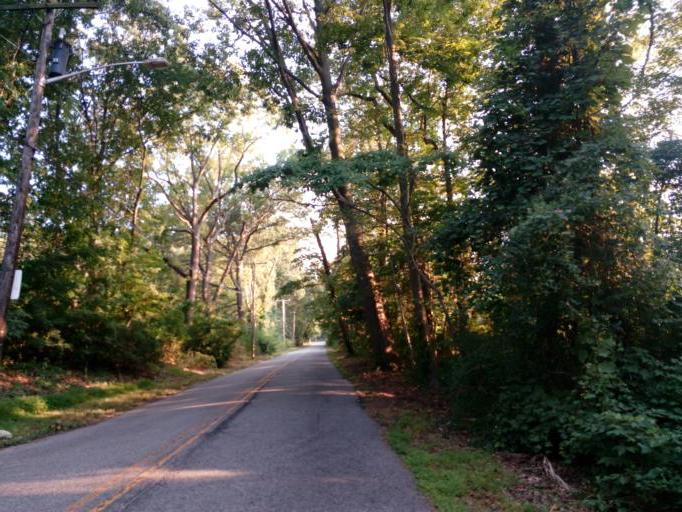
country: US
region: New York
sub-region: Nassau County
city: Lattingtown
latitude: 40.8927
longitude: -73.6181
